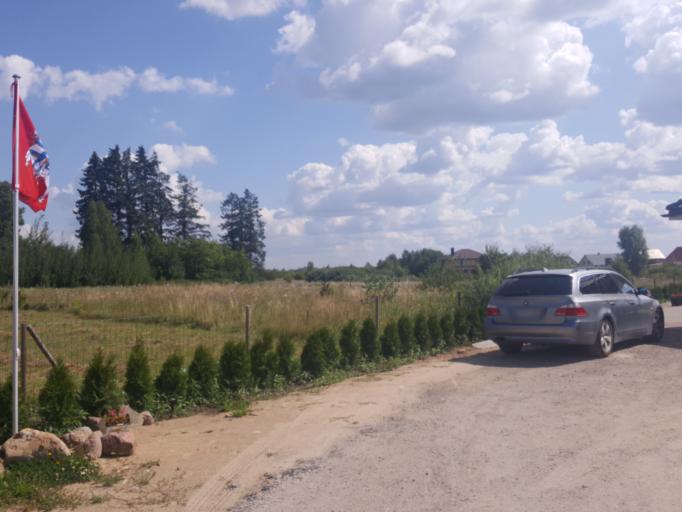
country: LT
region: Alytaus apskritis
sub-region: Alytus
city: Alytus
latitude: 54.3980
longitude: 23.9850
